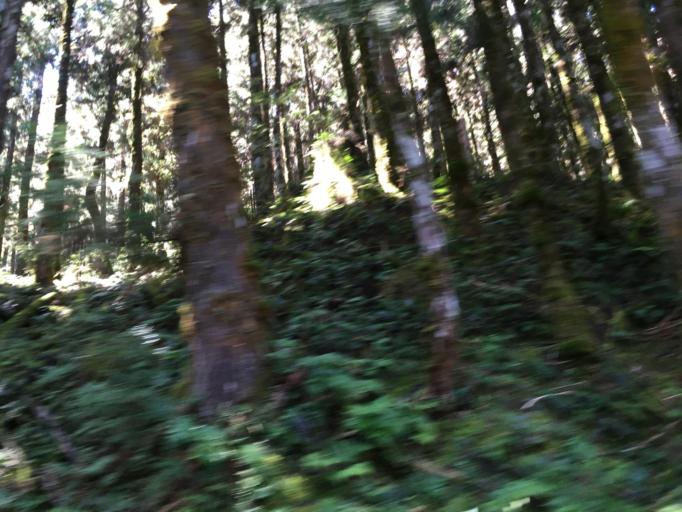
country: TW
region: Taiwan
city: Daxi
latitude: 24.5477
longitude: 121.4009
